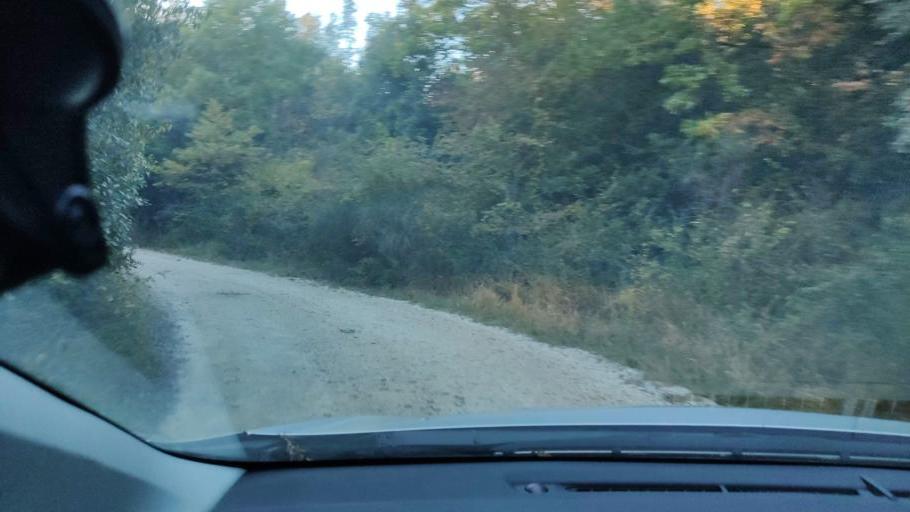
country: IT
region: Umbria
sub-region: Provincia di Terni
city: Amelia
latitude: 42.5824
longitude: 12.4341
